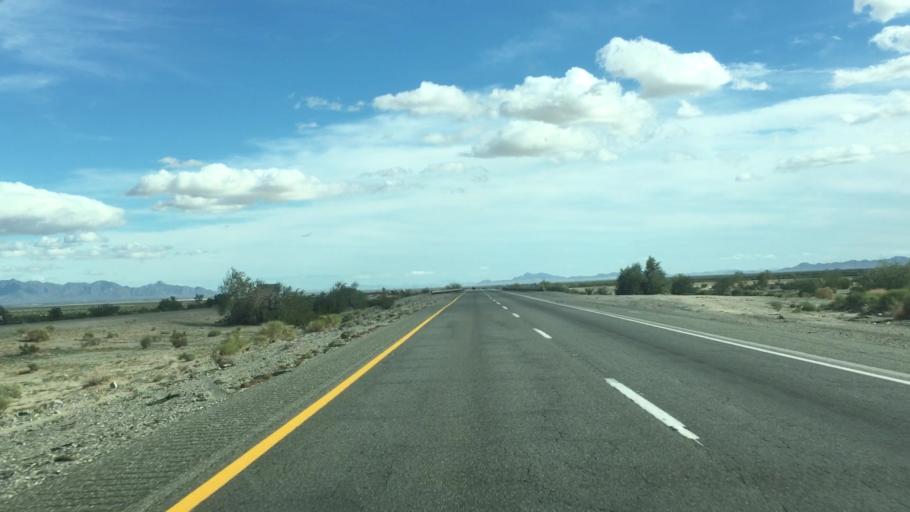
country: US
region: California
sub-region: Riverside County
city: Mesa Verde
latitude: 33.6523
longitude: -115.1422
